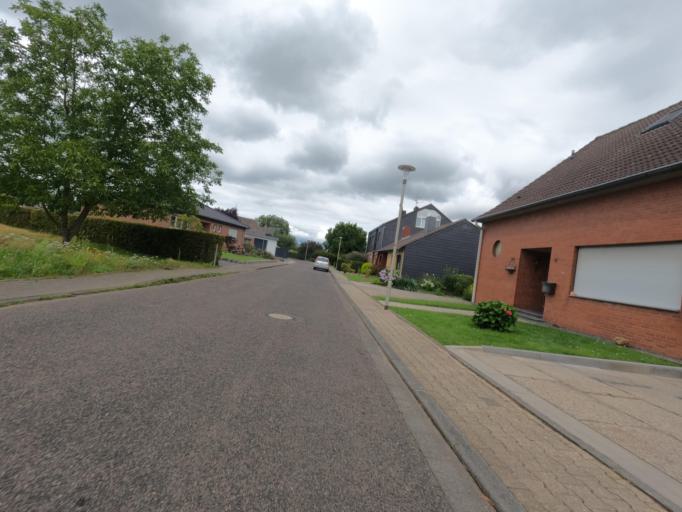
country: DE
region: North Rhine-Westphalia
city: Baesweiler
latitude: 50.9513
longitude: 6.1785
